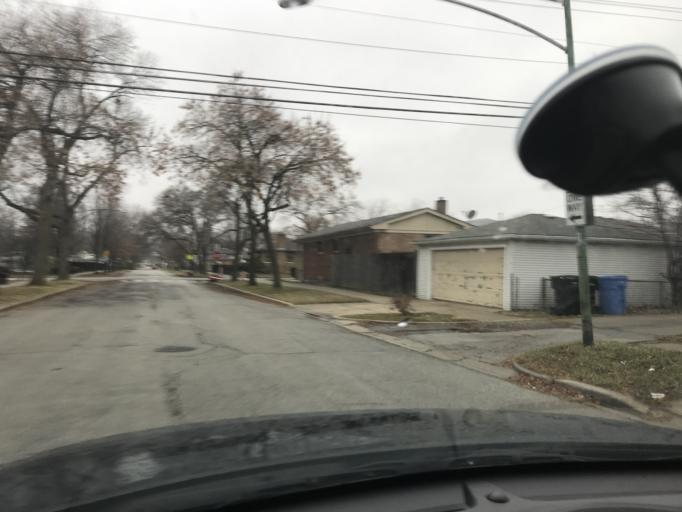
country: US
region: Illinois
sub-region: Cook County
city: Evergreen Park
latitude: 41.7253
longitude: -87.6376
